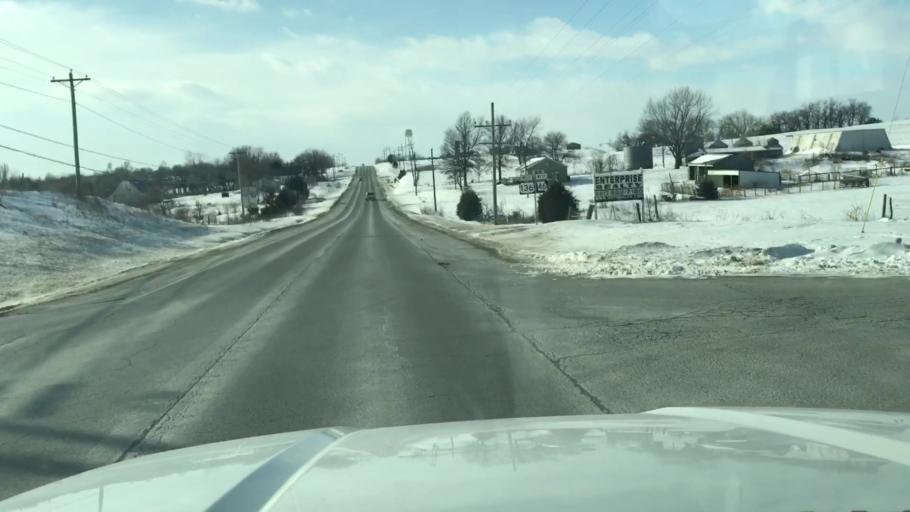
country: US
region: Missouri
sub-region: Nodaway County
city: Maryville
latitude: 40.3446
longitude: -94.7983
